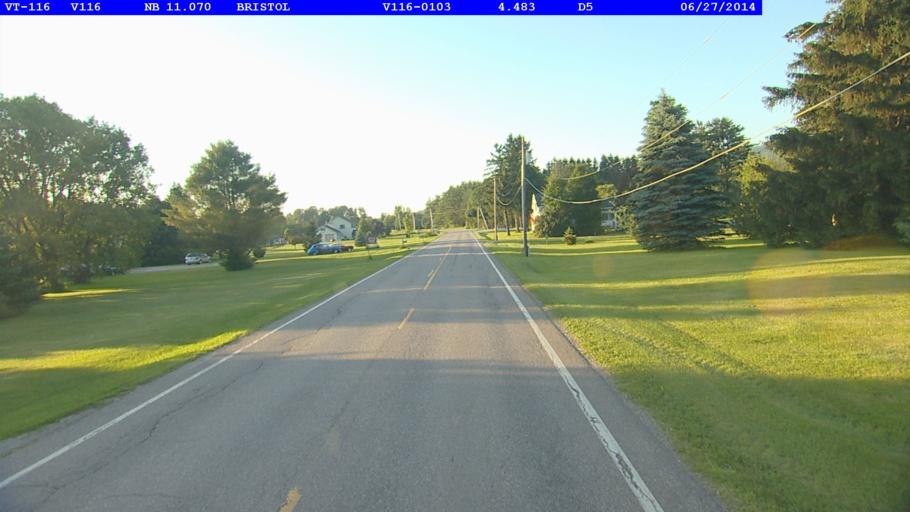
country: US
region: Vermont
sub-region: Addison County
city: Bristol
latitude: 44.1149
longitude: -73.0962
